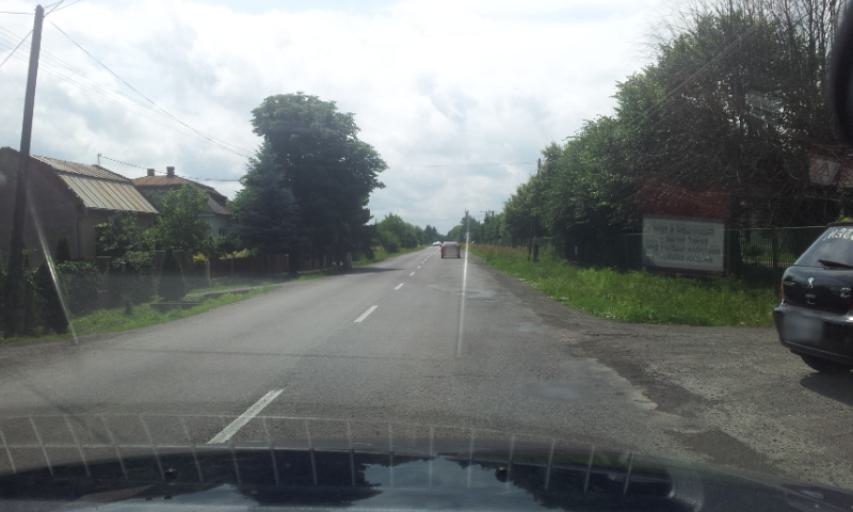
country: SK
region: Kosicky
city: Michalovce
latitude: 48.6527
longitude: 21.9937
